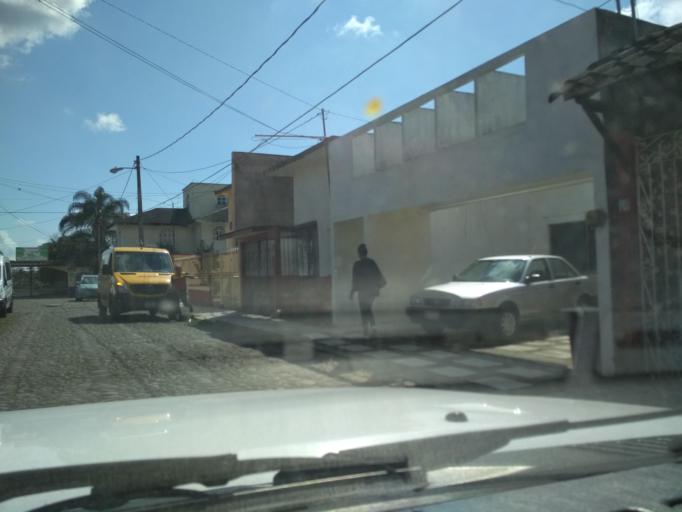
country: MX
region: Veracruz
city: Coatepec
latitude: 19.4500
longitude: -96.9500
